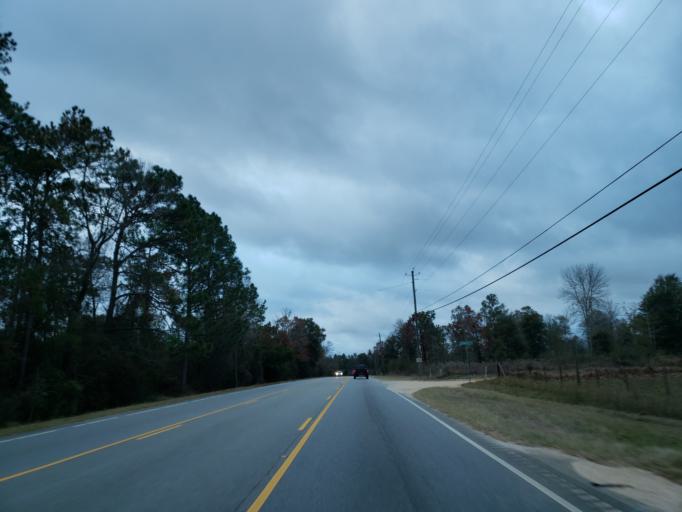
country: US
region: Mississippi
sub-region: Jackson County
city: Hurley
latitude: 30.8417
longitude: -88.3950
